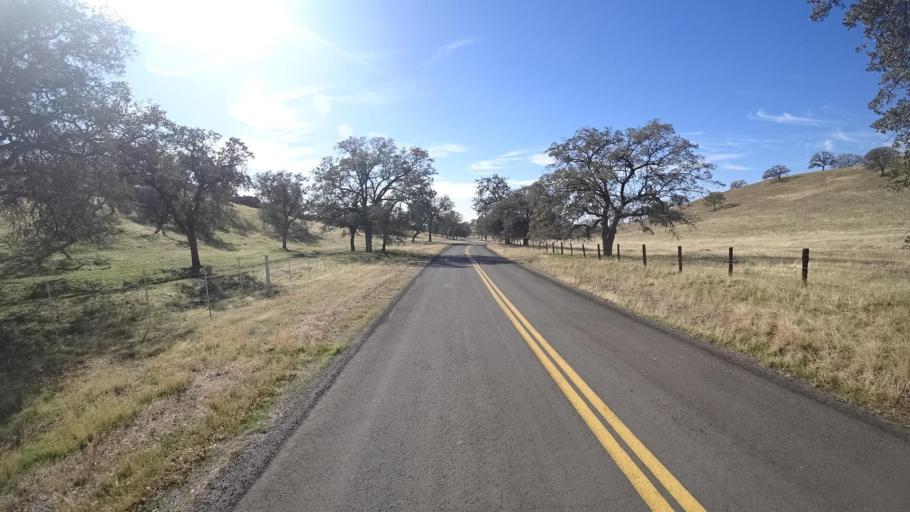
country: US
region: California
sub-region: Tulare County
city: Richgrove
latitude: 35.6837
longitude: -118.8431
